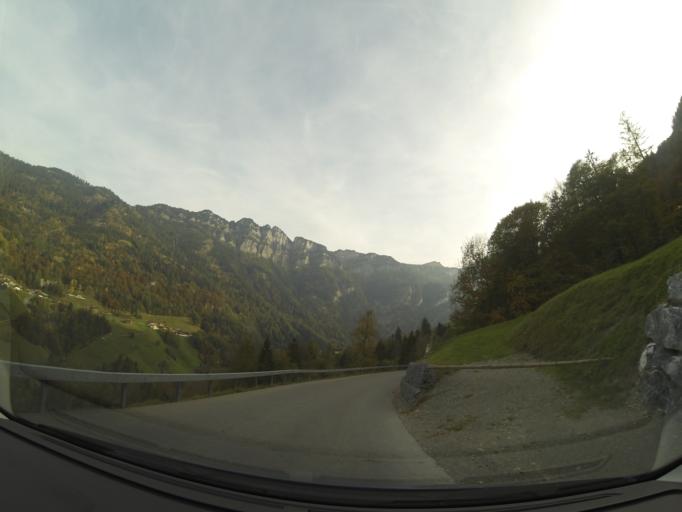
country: CH
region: Saint Gallen
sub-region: Wahlkreis Sarganserland
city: Bad Ragaz
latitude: 46.9574
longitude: 9.4740
